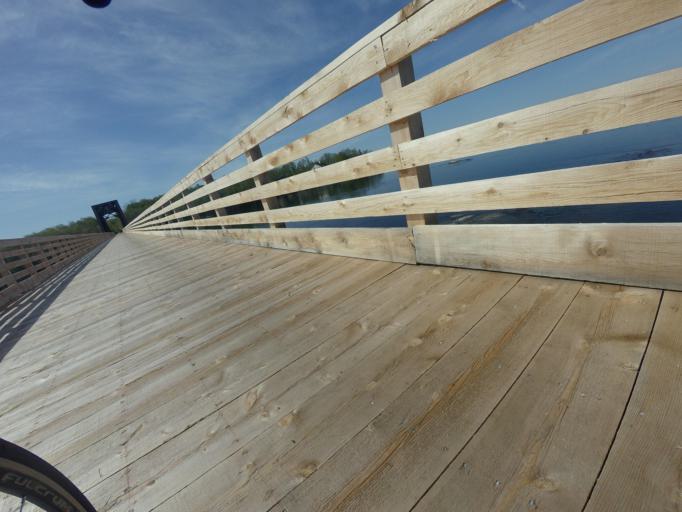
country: CA
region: Ontario
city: Arnprior
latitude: 45.4661
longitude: -76.2860
